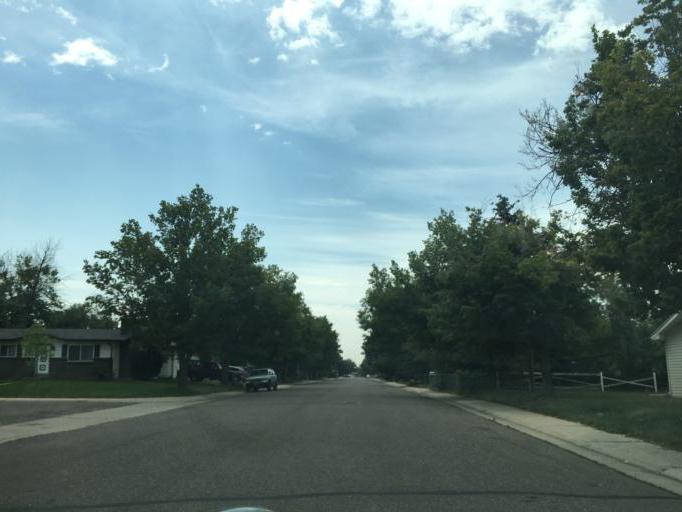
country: US
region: Colorado
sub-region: Adams County
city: Aurora
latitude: 39.7357
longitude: -104.7960
